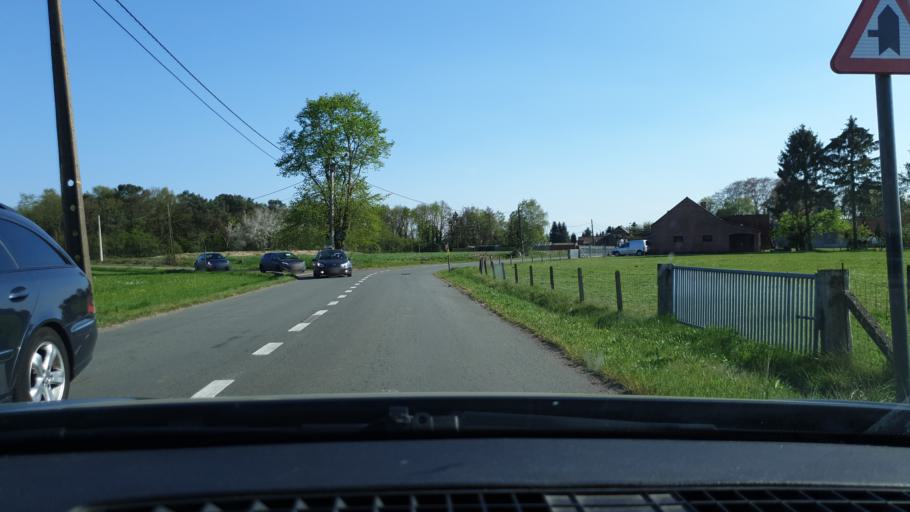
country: BE
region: Flanders
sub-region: Provincie Antwerpen
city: Geel
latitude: 51.1799
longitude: 4.9369
